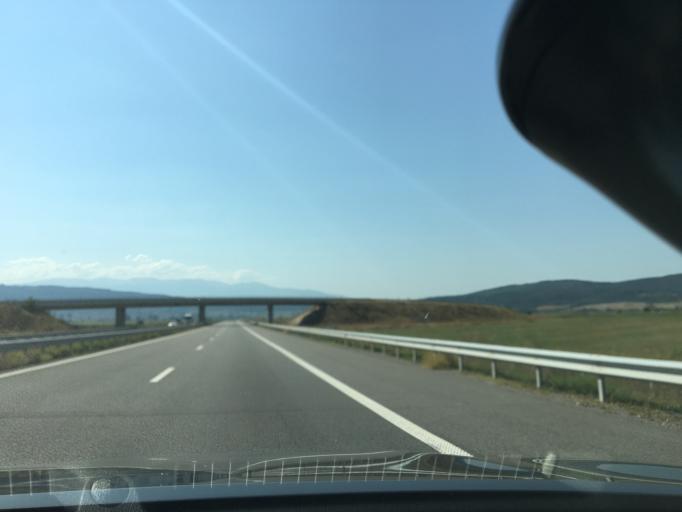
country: BG
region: Kyustendil
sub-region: Obshtina Bobovdol
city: Bobovdol
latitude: 42.4331
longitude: 23.1136
